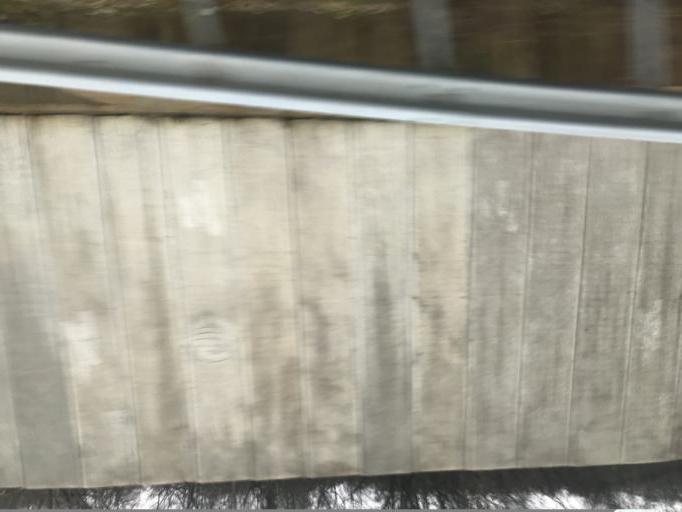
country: TR
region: Bartin
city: Amasra
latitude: 41.7295
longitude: 32.3827
